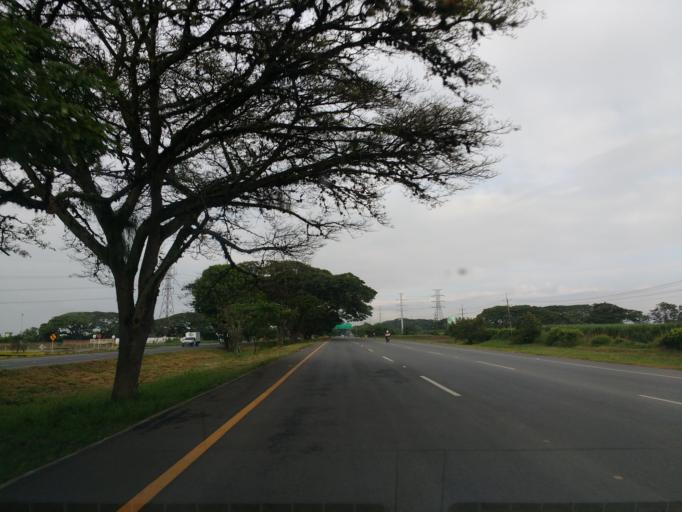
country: CO
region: Valle del Cauca
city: Yumbo
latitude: 3.5064
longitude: -76.4188
